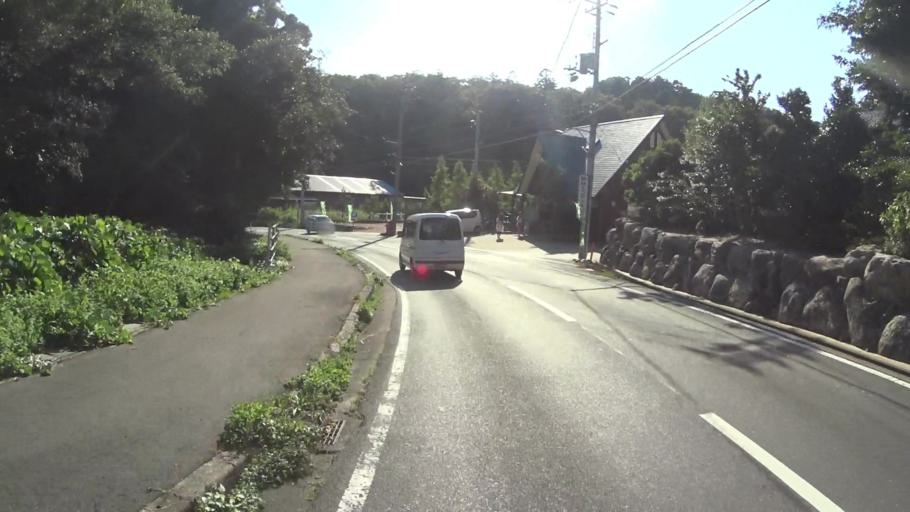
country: JP
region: Kyoto
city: Miyazu
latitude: 35.6955
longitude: 135.0468
